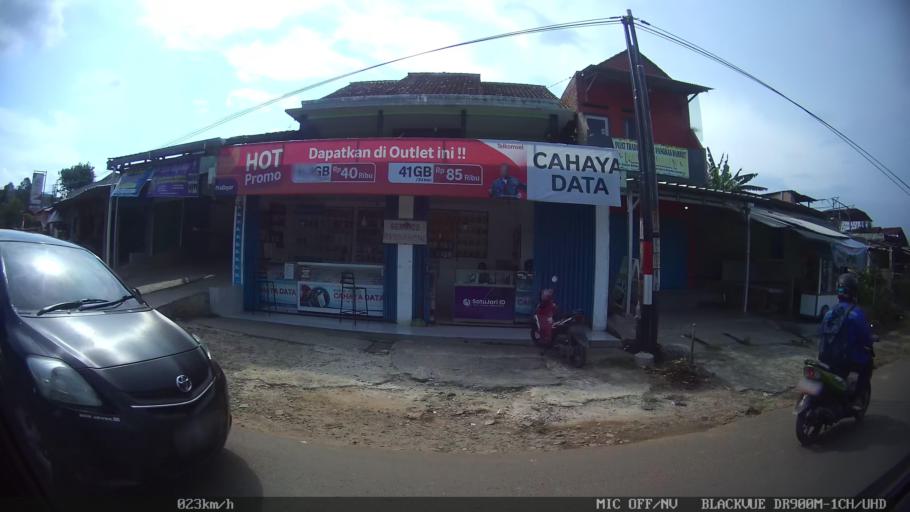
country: ID
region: Lampung
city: Bandarlampung
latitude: -5.4064
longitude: 105.2282
